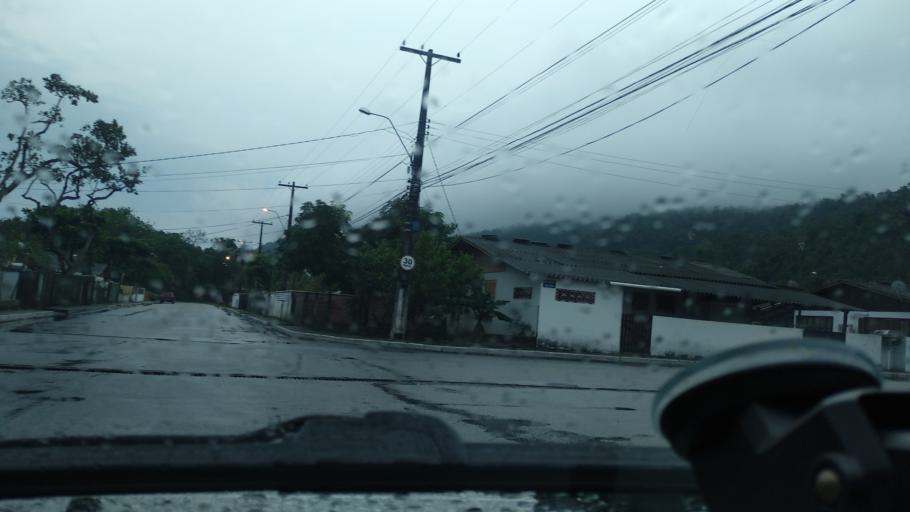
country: BR
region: Rio de Janeiro
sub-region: Angra Dos Reis
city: Angra dos Reis
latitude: -23.0330
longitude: -44.5522
